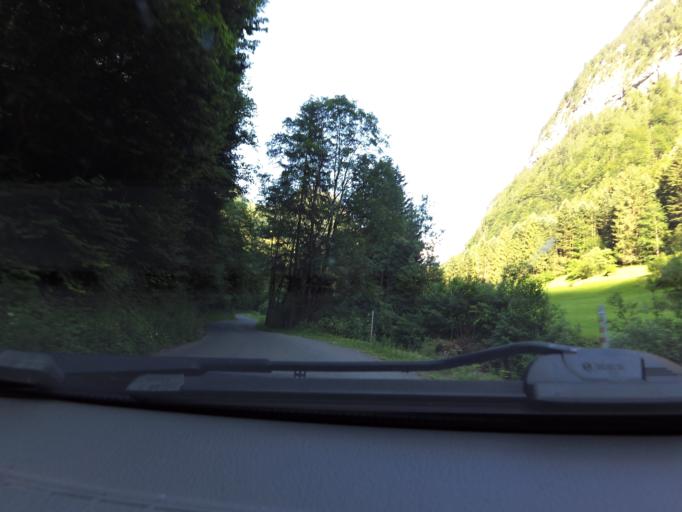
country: CH
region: Uri
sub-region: Uri
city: Bauen
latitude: 46.9116
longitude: 8.5415
